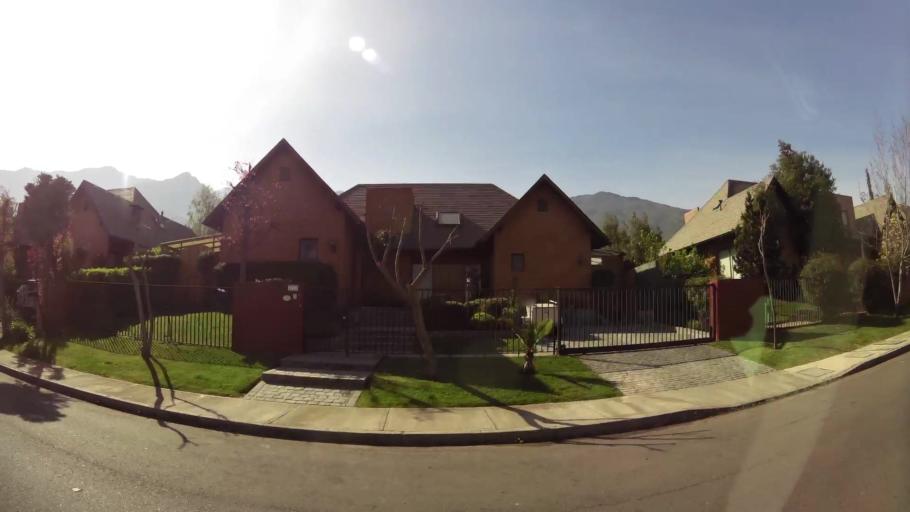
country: CL
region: Santiago Metropolitan
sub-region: Provincia de Santiago
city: Villa Presidente Frei, Nunoa, Santiago, Chile
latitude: -33.4988
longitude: -70.5265
